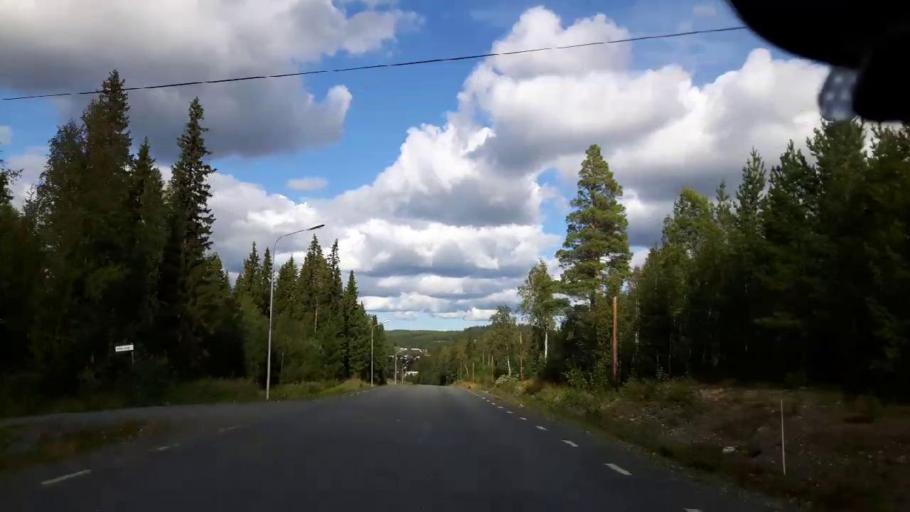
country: SE
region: Jaemtland
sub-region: Braecke Kommun
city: Braecke
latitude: 63.2874
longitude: 15.5866
